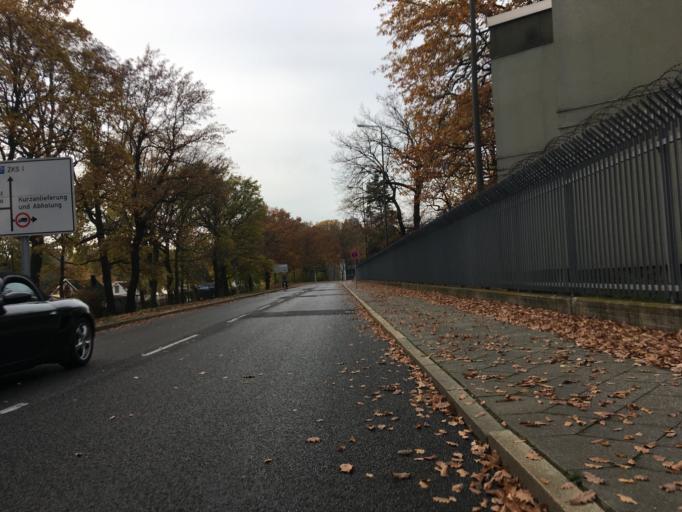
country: DE
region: Berlin
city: Charlottenburg-Nord
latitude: 52.5508
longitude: 13.2881
